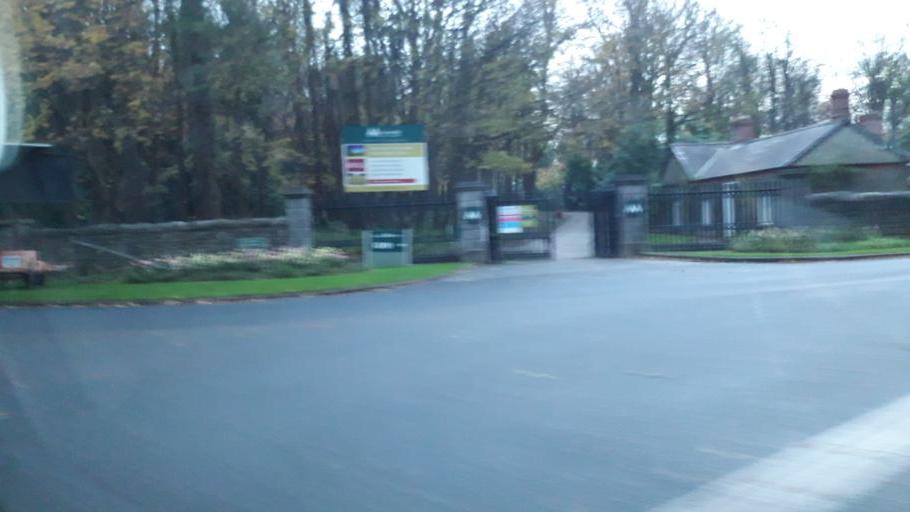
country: IE
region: Leinster
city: Malahide
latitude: 53.4403
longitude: -6.1765
